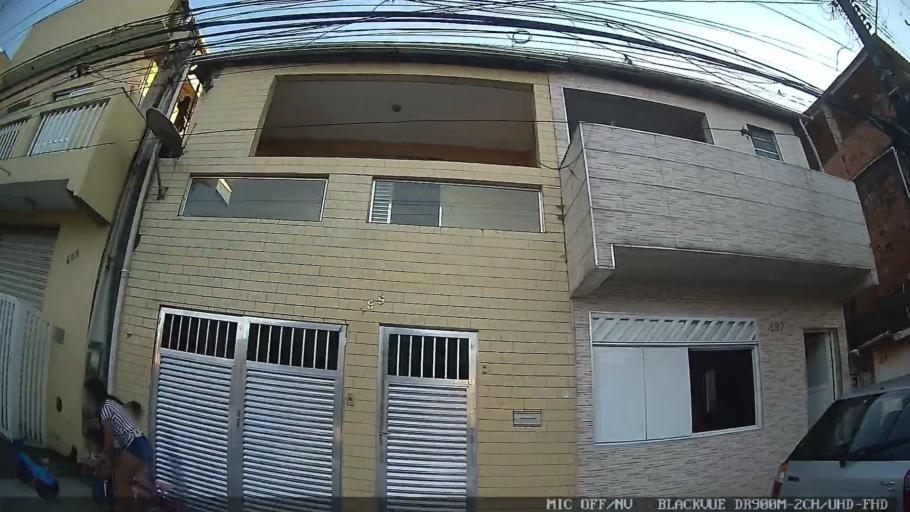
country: BR
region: Sao Paulo
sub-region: Guaruja
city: Guaruja
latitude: -23.9885
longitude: -46.2737
